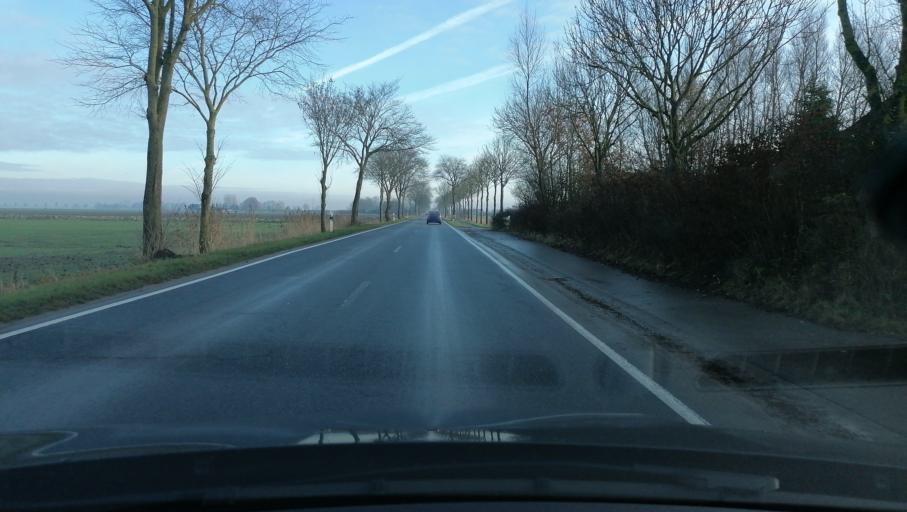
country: DE
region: Schleswig-Holstein
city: Wohrden
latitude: 54.1214
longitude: 8.9988
